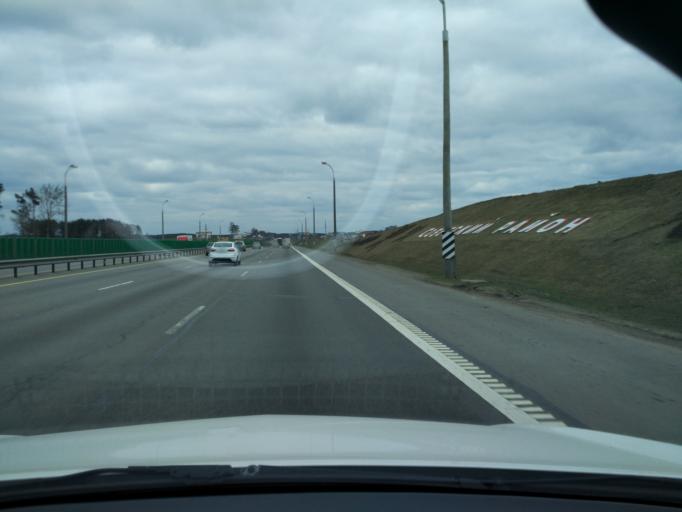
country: BY
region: Minsk
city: Bal'shavik
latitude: 53.9702
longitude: 27.5608
